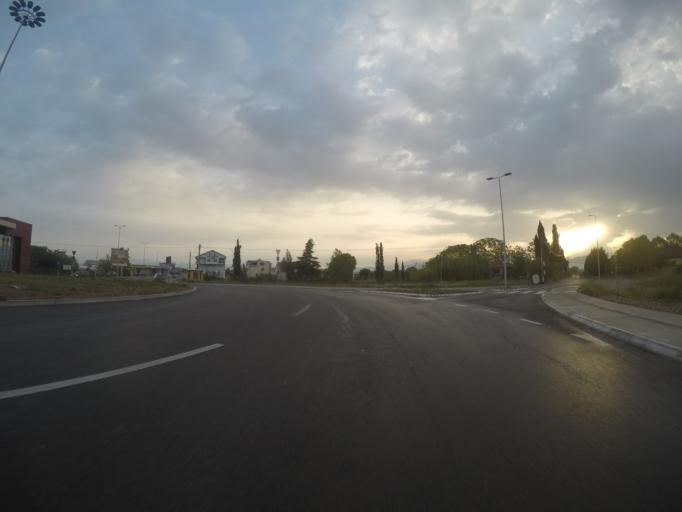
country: ME
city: Mojanovici
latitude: 42.3550
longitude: 19.2232
